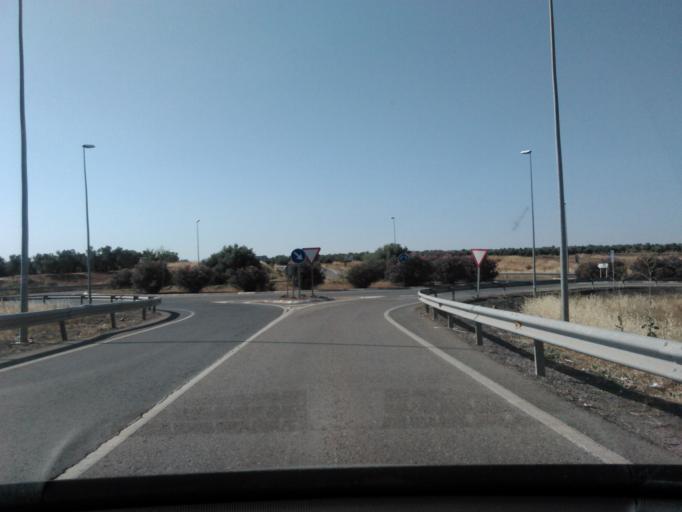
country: ES
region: Andalusia
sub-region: Provincia de Jaen
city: La Carolina
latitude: 38.2814
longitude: -3.5940
